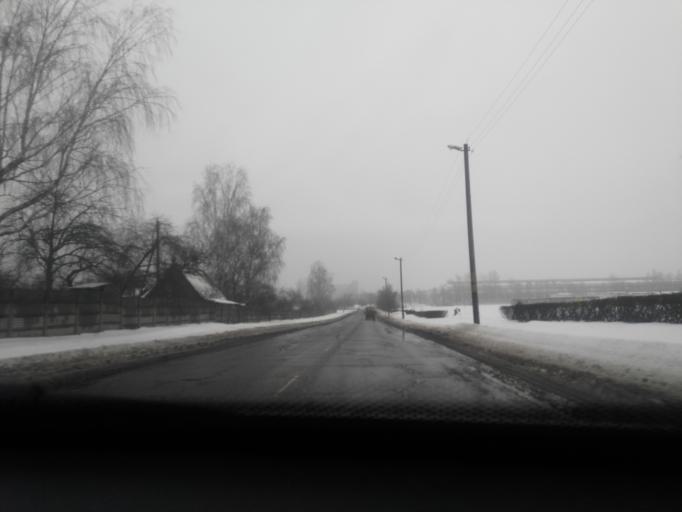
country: BY
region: Mogilev
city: Babruysk
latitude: 53.1869
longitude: 29.2125
